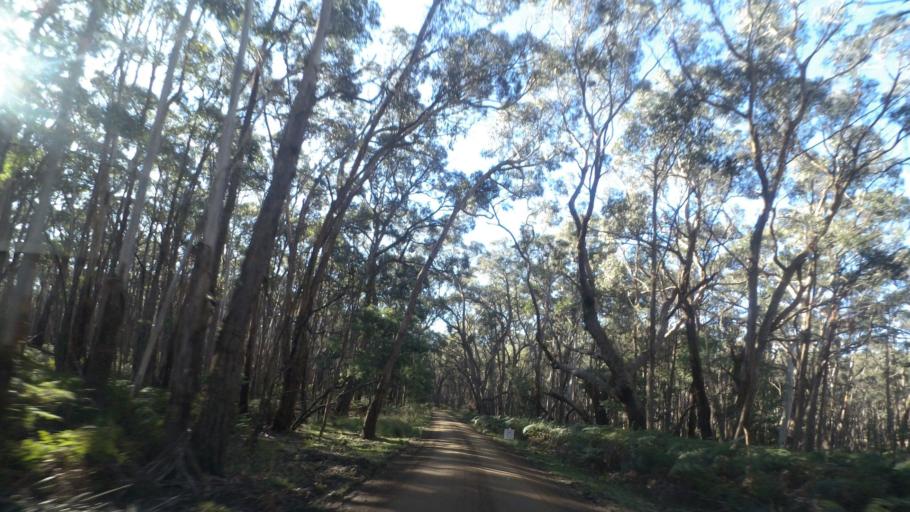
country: AU
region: Victoria
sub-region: Mount Alexander
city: Castlemaine
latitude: -37.2855
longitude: 144.3318
